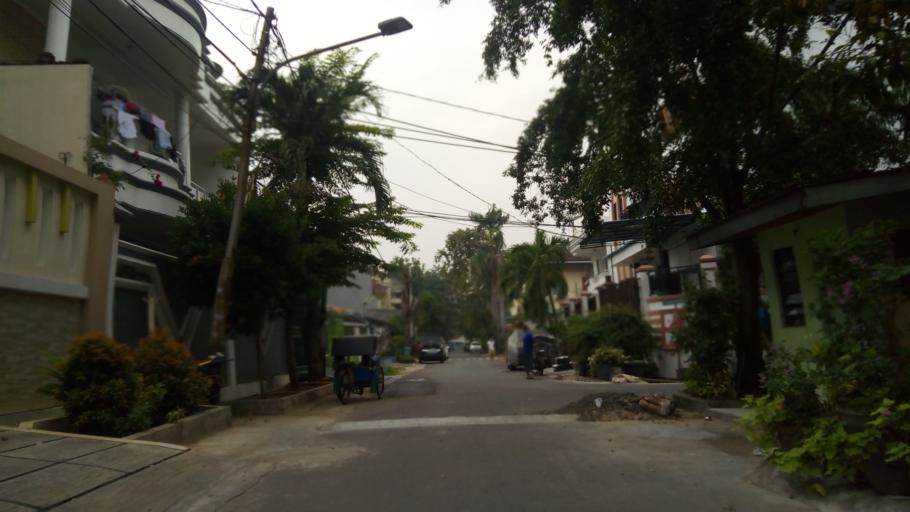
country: ID
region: Jakarta Raya
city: Jakarta
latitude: -6.1436
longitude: 106.8401
